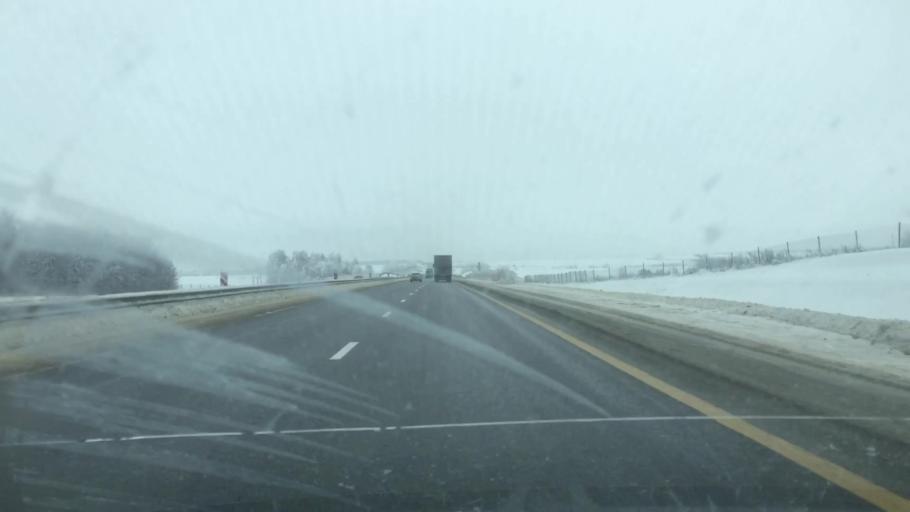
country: RU
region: Tula
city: Kazachka
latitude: 53.3412
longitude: 38.1811
